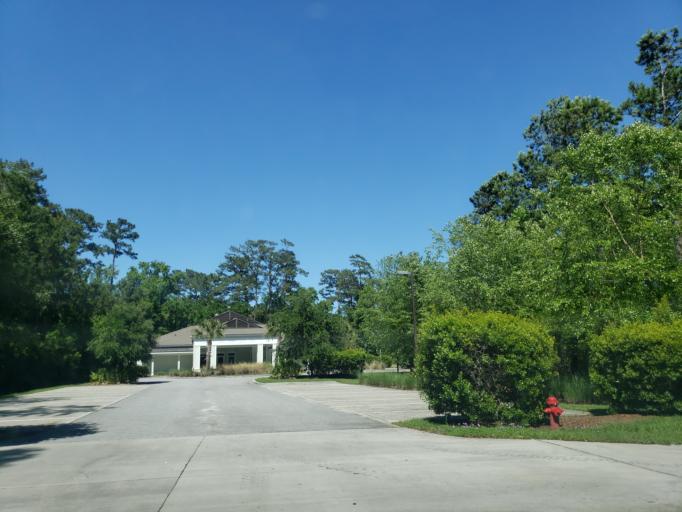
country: US
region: Georgia
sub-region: Chatham County
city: Isle of Hope
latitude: 31.9848
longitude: -81.0714
